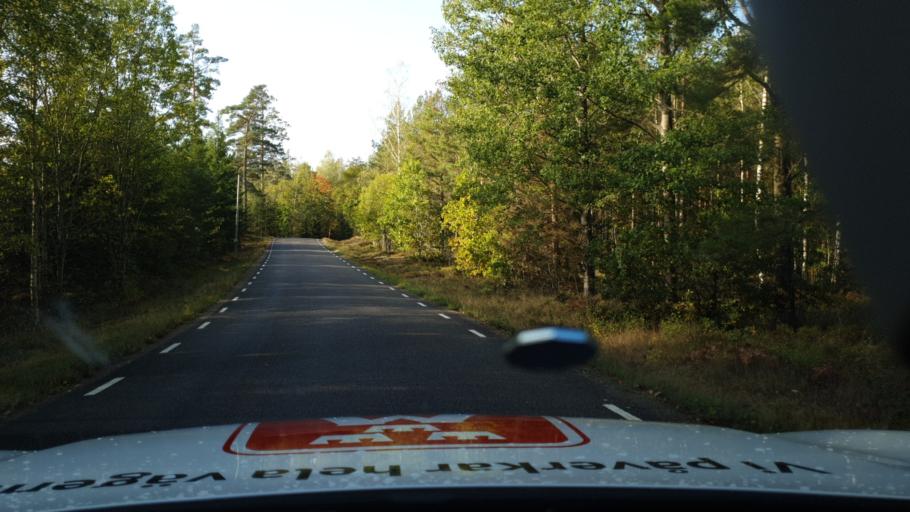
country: SE
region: Kalmar
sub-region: Vasterviks Kommun
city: Overum
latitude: 57.9906
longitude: 16.3382
